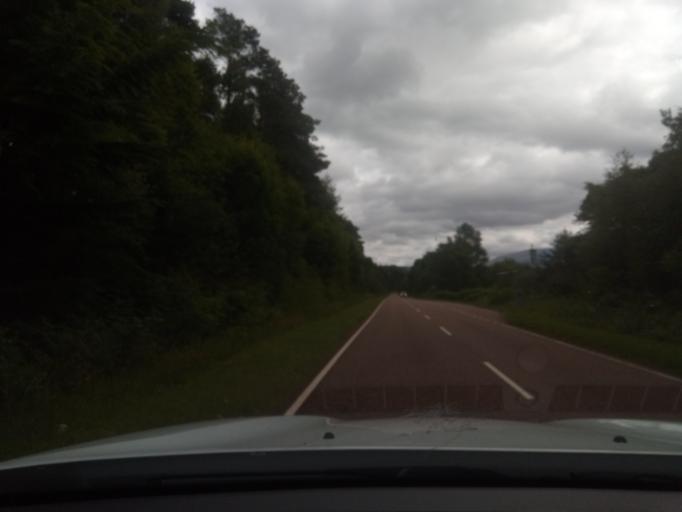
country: GB
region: Scotland
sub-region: Highland
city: Fort William
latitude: 56.8558
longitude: -5.2070
